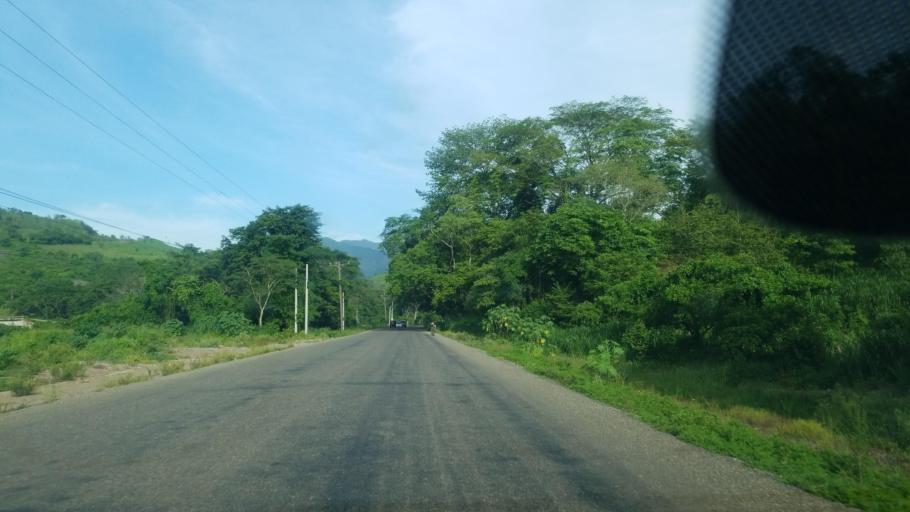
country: HN
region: Santa Barbara
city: Trinidad
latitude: 15.1320
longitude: -88.2140
